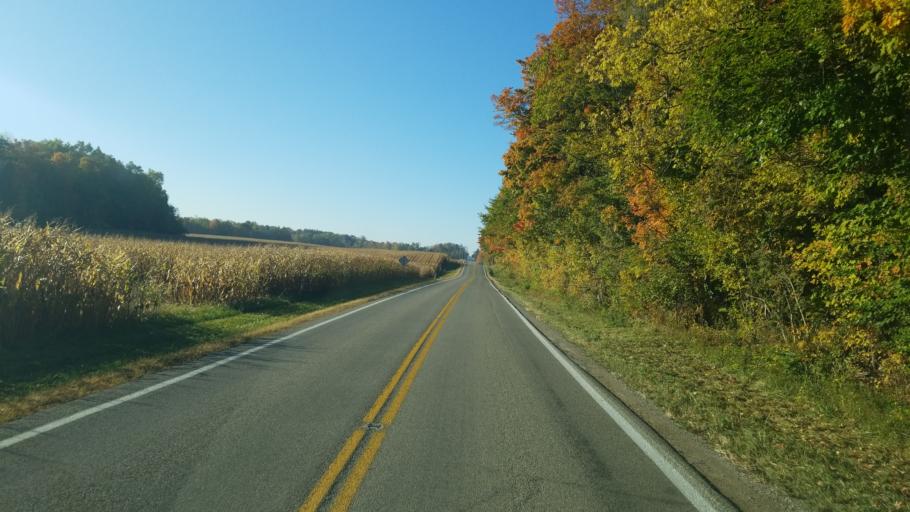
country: US
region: Ohio
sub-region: Knox County
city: Centerburg
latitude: 40.4172
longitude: -82.7032
